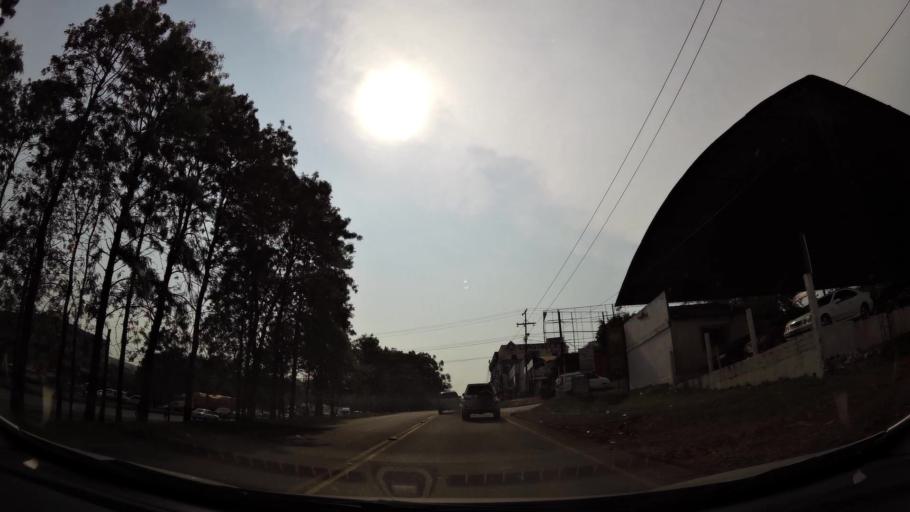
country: PY
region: Alto Parana
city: Ciudad del Este
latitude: -25.5023
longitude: -54.6524
